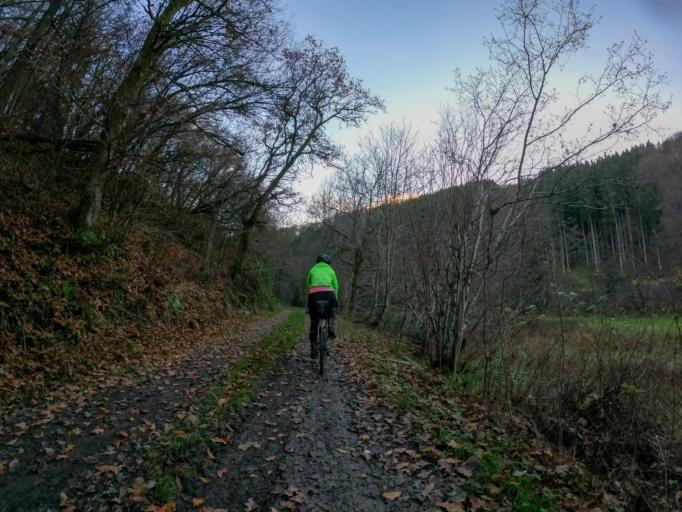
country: LU
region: Diekirch
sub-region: Canton de Wiltz
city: Bavigne
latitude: 49.9428
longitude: 5.8333
